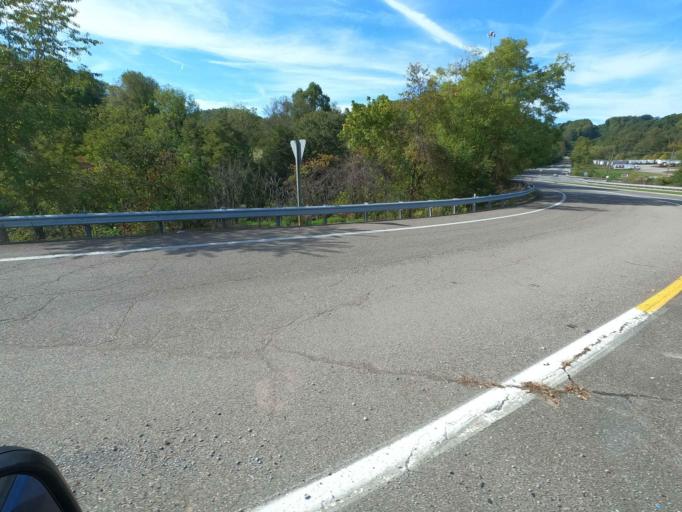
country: US
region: Tennessee
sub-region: Sullivan County
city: Walnut Hill
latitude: 36.6031
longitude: -82.2320
